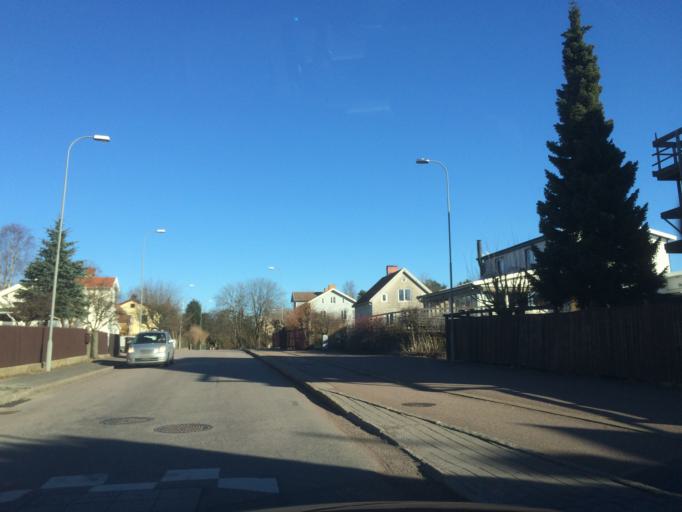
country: SE
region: Vaestra Goetaland
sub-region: Goteborg
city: Majorna
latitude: 57.6730
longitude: 11.8967
